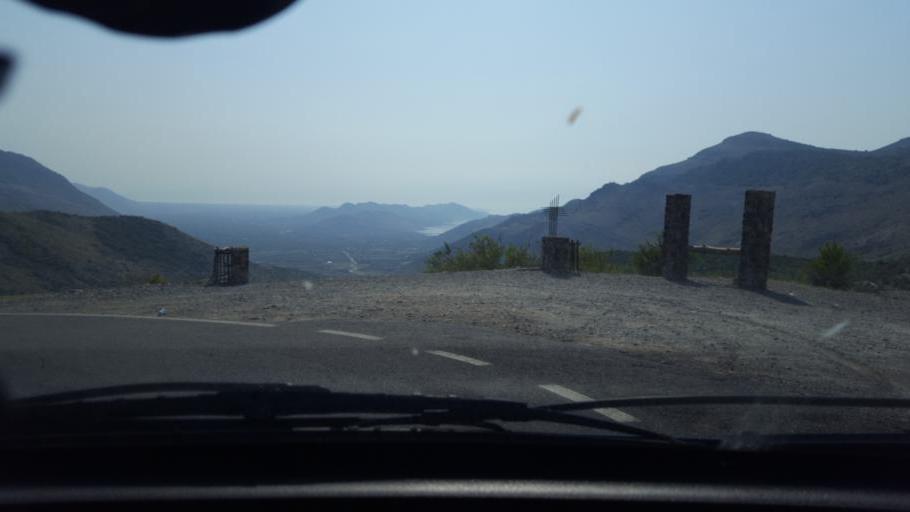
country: AL
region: Shkoder
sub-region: Rrethi i Malesia e Madhe
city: Hot
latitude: 42.3753
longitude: 19.4504
